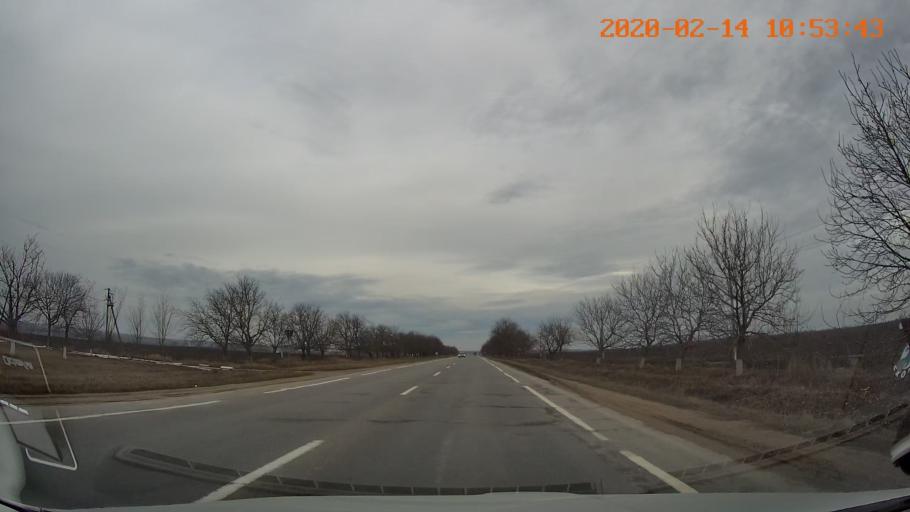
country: MD
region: Raionul Edinet
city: Edinet
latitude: 48.1040
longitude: 27.4116
